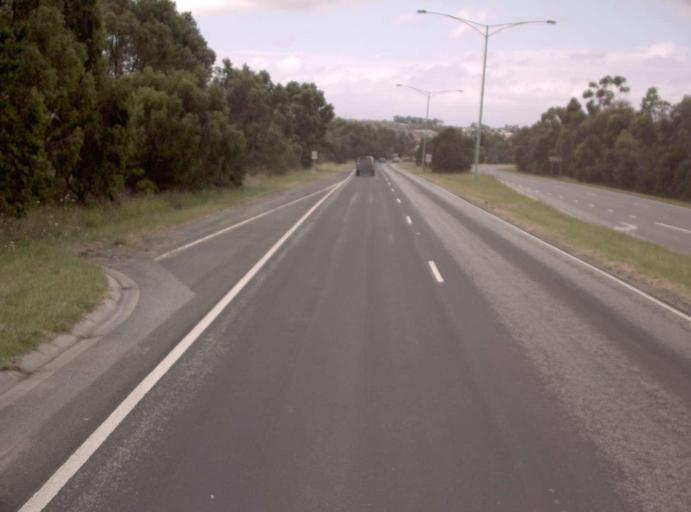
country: AU
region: Victoria
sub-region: Cardinia
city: Pakenham Upper
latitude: -38.0678
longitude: 145.4973
